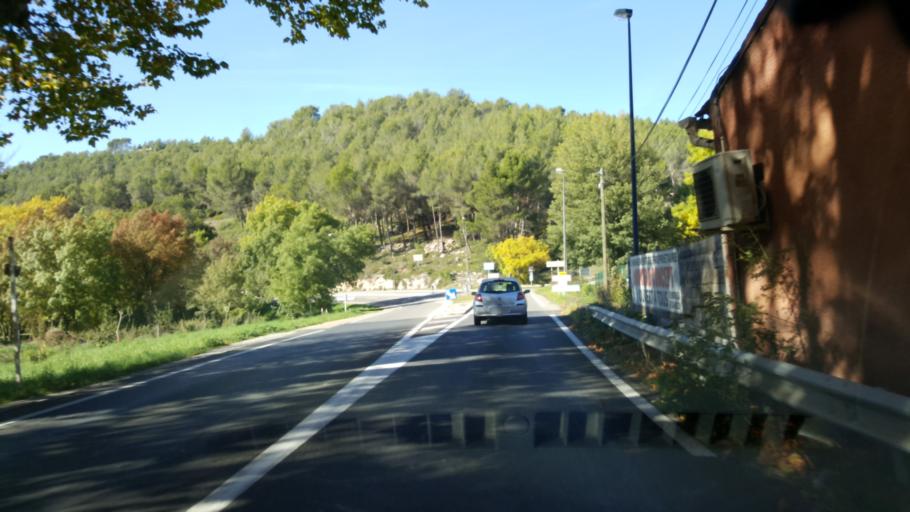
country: FR
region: Provence-Alpes-Cote d'Azur
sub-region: Departement du Var
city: Saint-Zacharie
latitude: 43.3870
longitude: 5.7206
